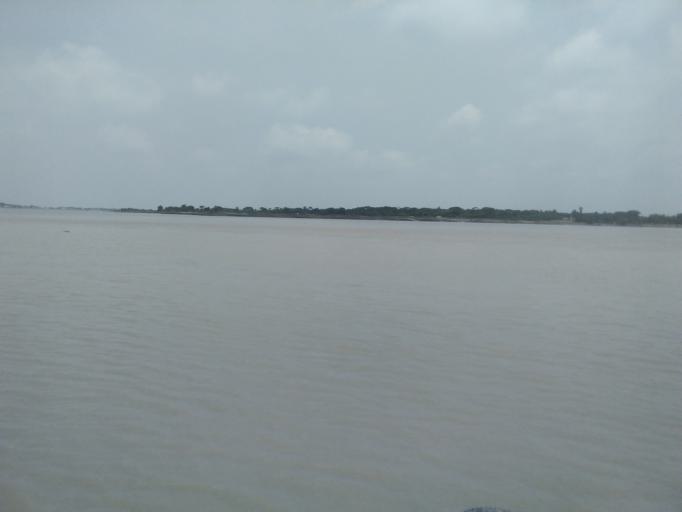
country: BD
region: Khulna
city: Phultala
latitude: 22.6418
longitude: 89.4133
